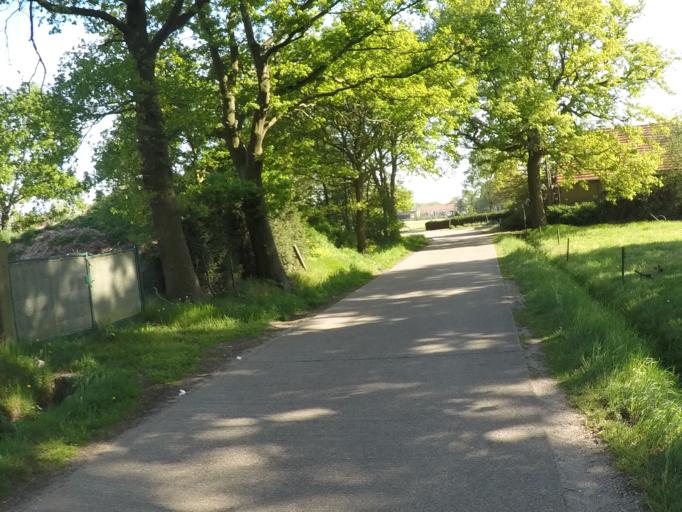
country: BE
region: Flanders
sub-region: Provincie Antwerpen
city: Nijlen
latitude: 51.1542
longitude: 4.7008
